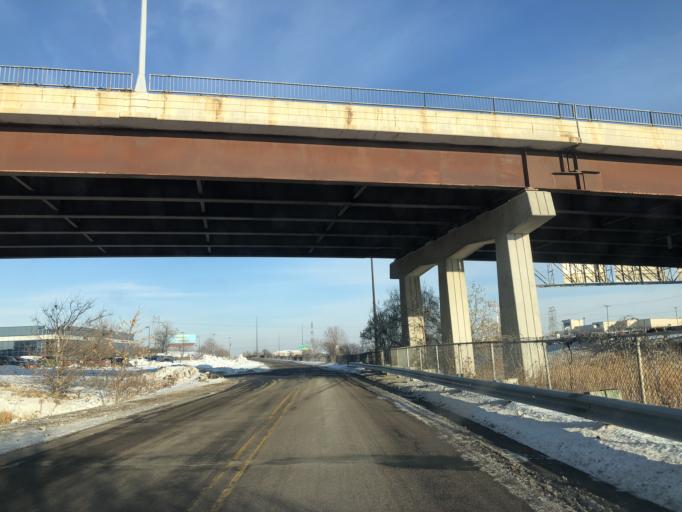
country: US
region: Minnesota
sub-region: Ramsey County
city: Lauderdale
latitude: 45.0144
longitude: -93.1881
